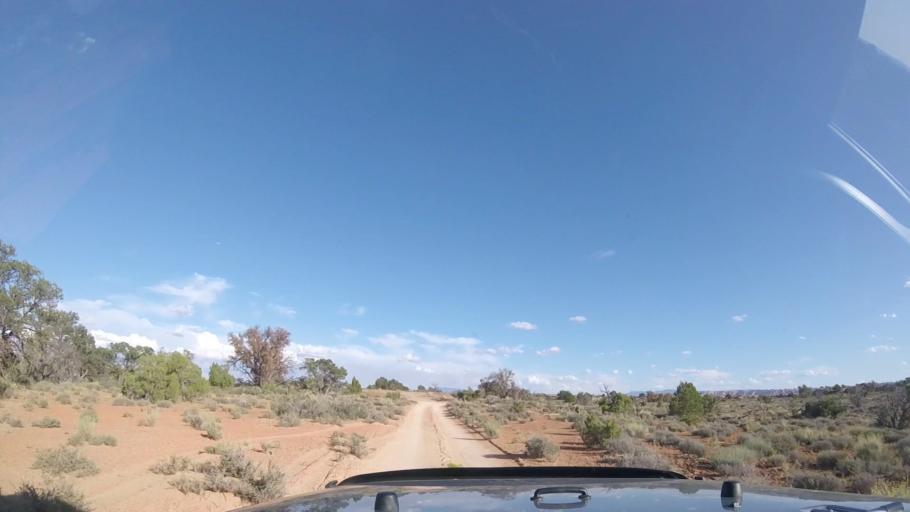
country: US
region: Utah
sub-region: Grand County
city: Moab
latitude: 38.2131
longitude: -109.8111
